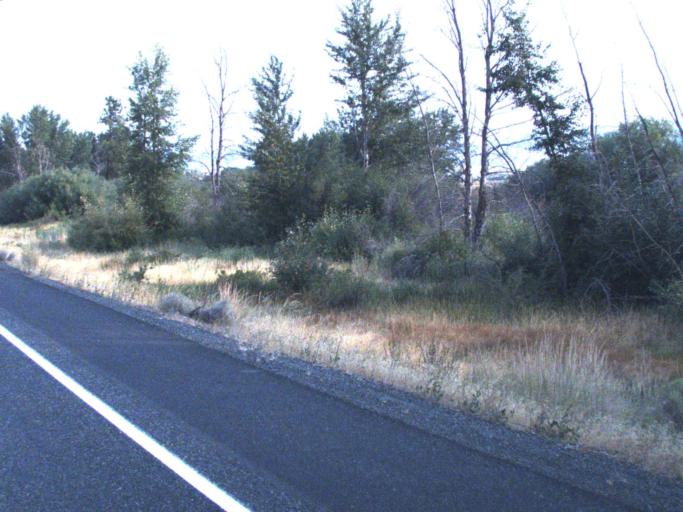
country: US
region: Washington
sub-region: Kittitas County
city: Ellensburg
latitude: 47.0987
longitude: -120.6595
